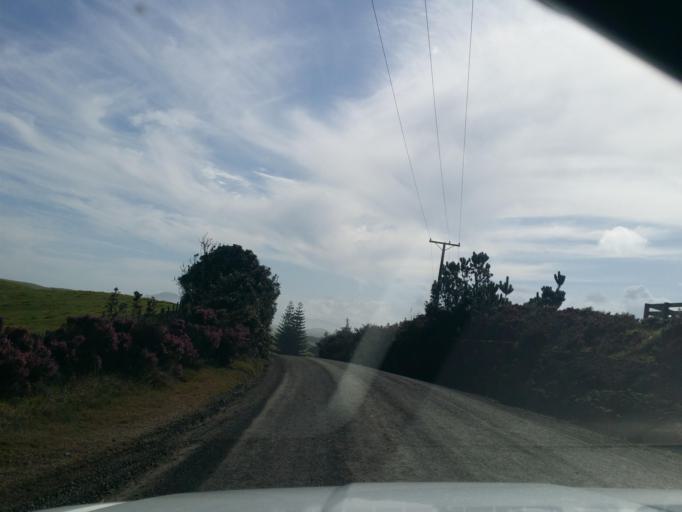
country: NZ
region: Northland
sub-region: Kaipara District
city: Dargaville
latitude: -35.8464
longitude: 173.6616
